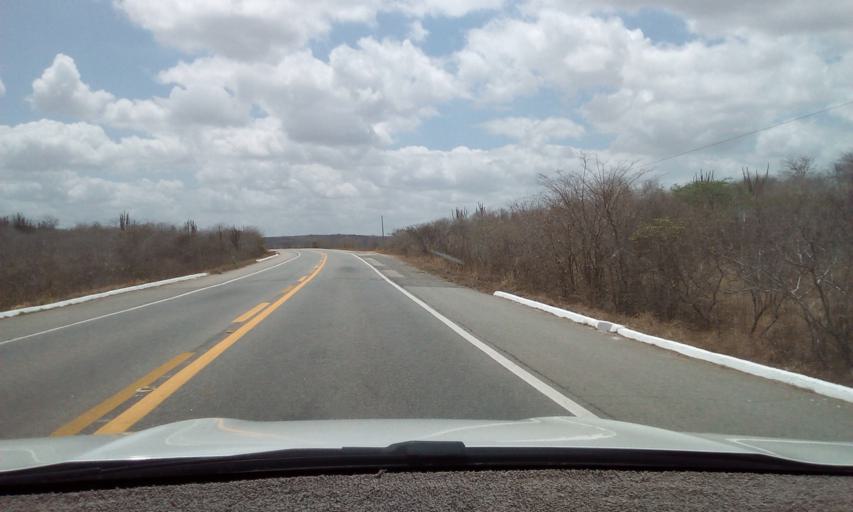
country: BR
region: Paraiba
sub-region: Boqueirao
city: Boqueirao
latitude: -7.6749
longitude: -36.0754
